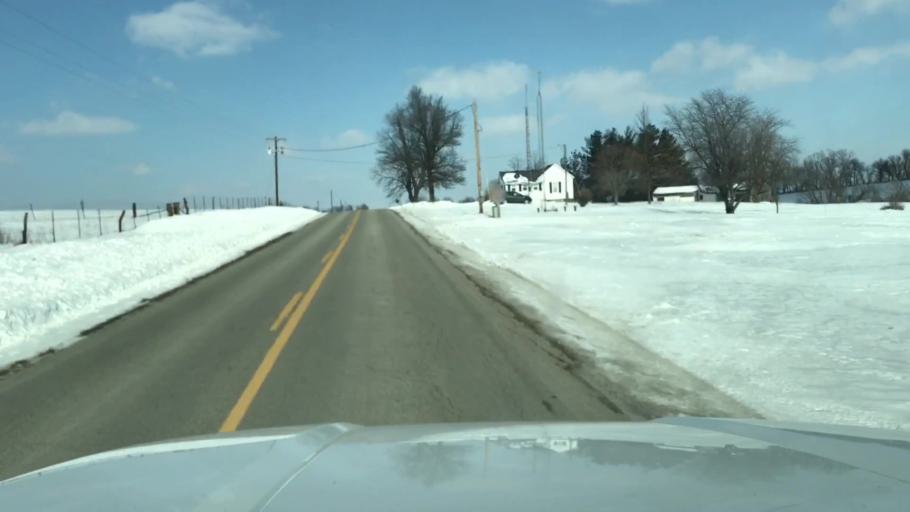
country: US
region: Missouri
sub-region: Nodaway County
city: Maryville
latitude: 40.3471
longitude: -94.7224
